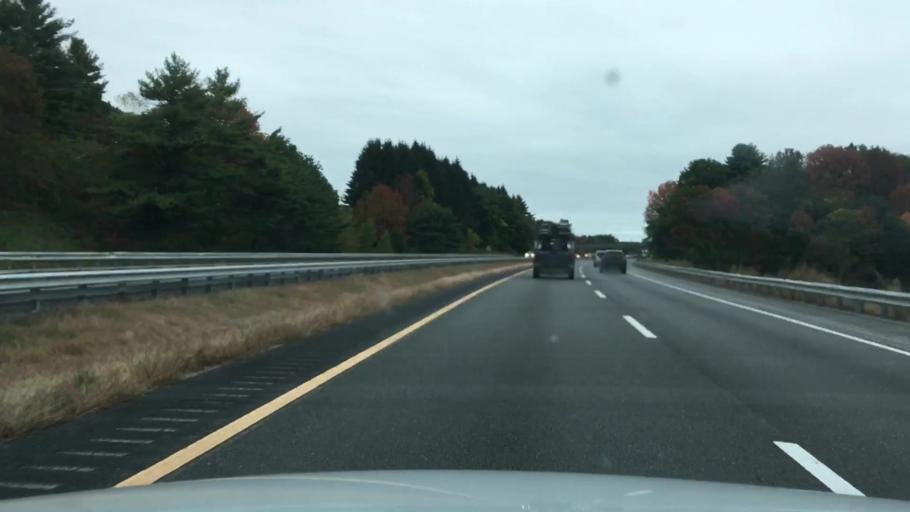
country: US
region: Maine
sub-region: Cumberland County
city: Falmouth
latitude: 43.7253
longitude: -70.2409
